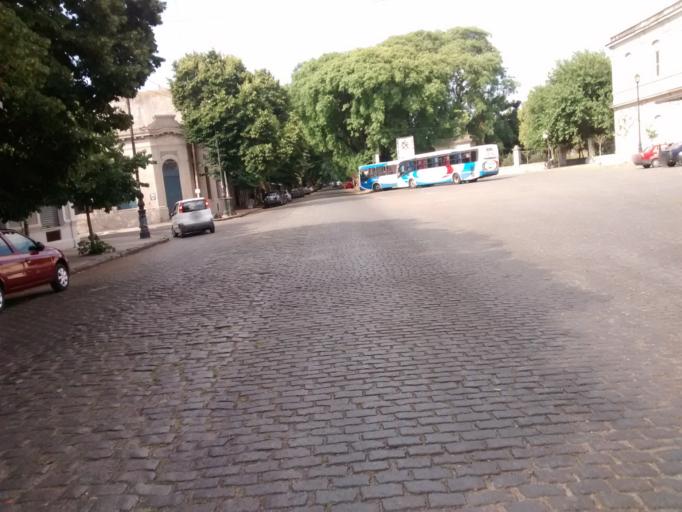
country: AR
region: Buenos Aires
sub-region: Partido de La Plata
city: La Plata
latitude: -34.9399
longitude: -57.9396
